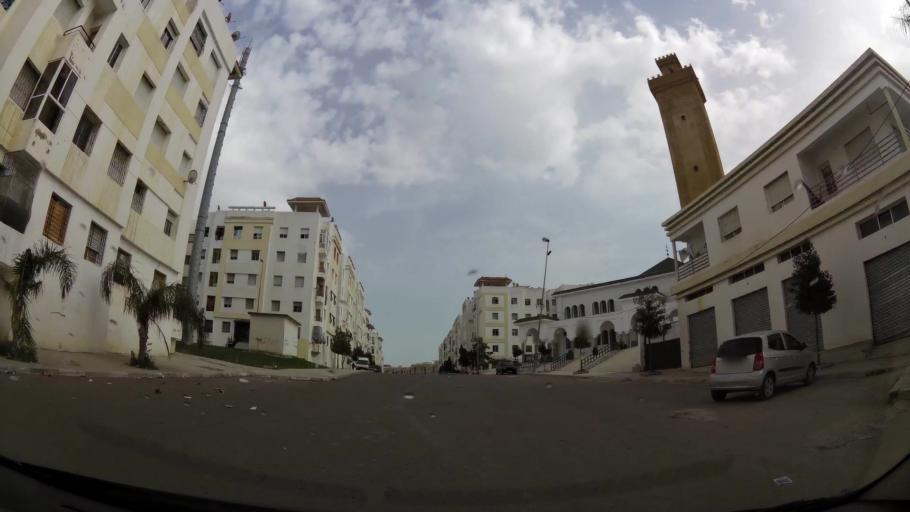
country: MA
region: Tanger-Tetouan
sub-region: Tanger-Assilah
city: Boukhalef
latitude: 35.7387
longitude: -5.8896
